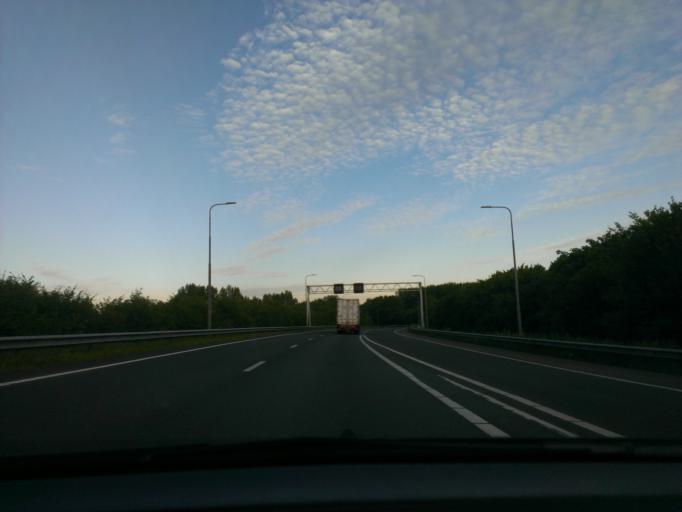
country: NL
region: South Holland
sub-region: Gemeente Ridderkerk
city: Ridderkerk
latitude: 51.8713
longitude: 4.5720
